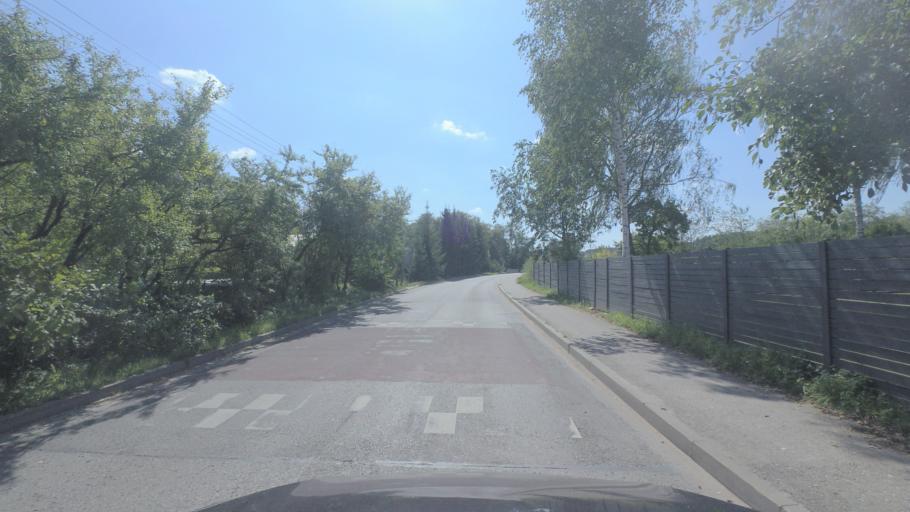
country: LT
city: Nemencine
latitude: 54.8332
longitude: 25.3684
